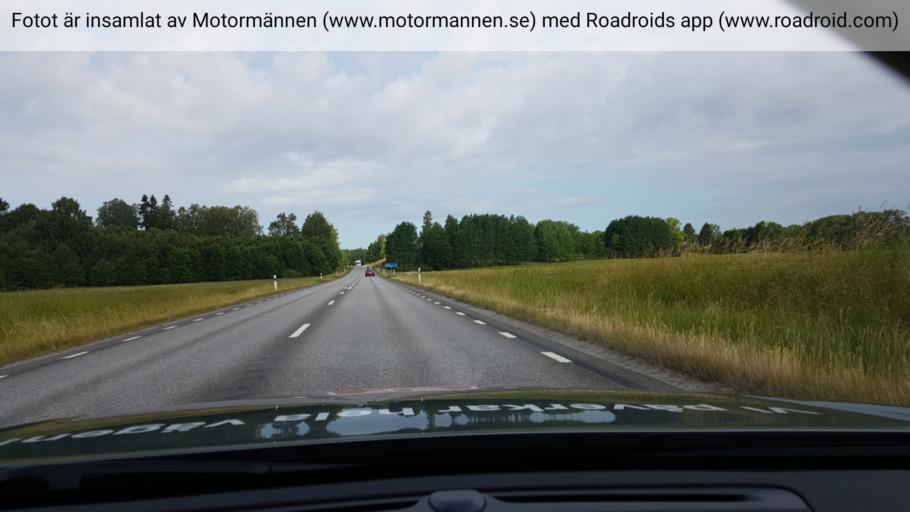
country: SE
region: OEstergoetland
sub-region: Motala Kommun
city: Borensberg
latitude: 58.5340
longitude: 15.3880
